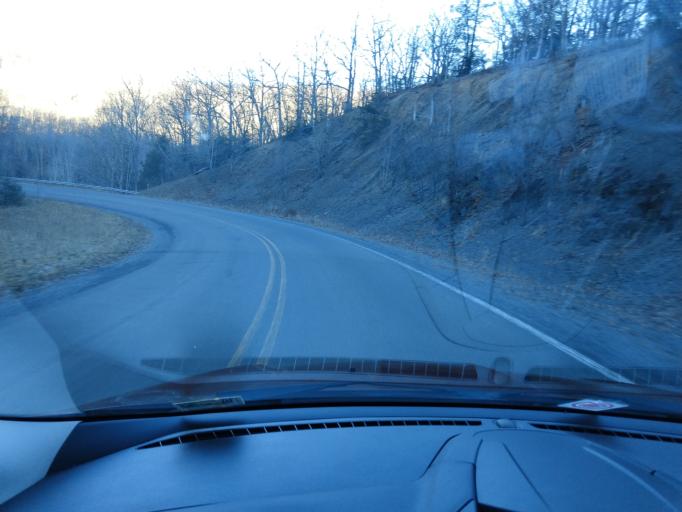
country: US
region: Virginia
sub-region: Highland County
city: Monterey
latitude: 38.4503
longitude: -79.6531
